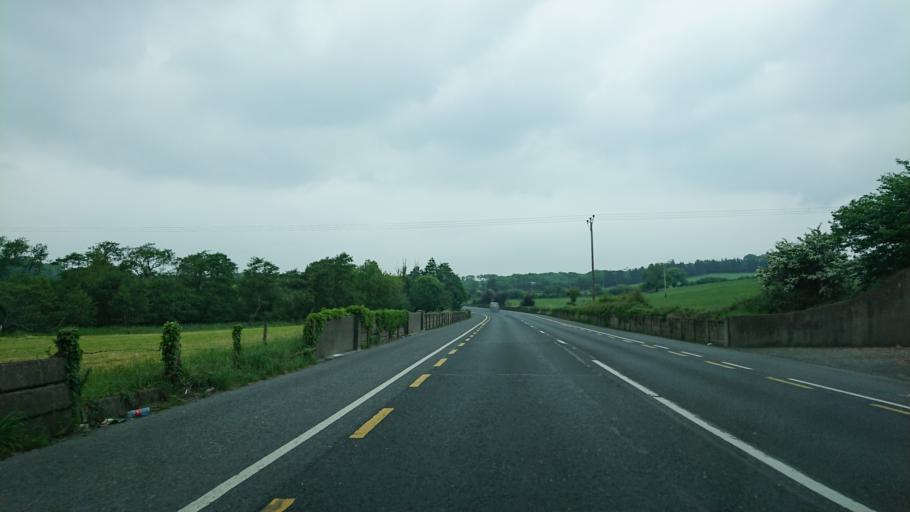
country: IE
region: Munster
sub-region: Waterford
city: Tra Mhor
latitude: 52.2014
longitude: -7.1175
